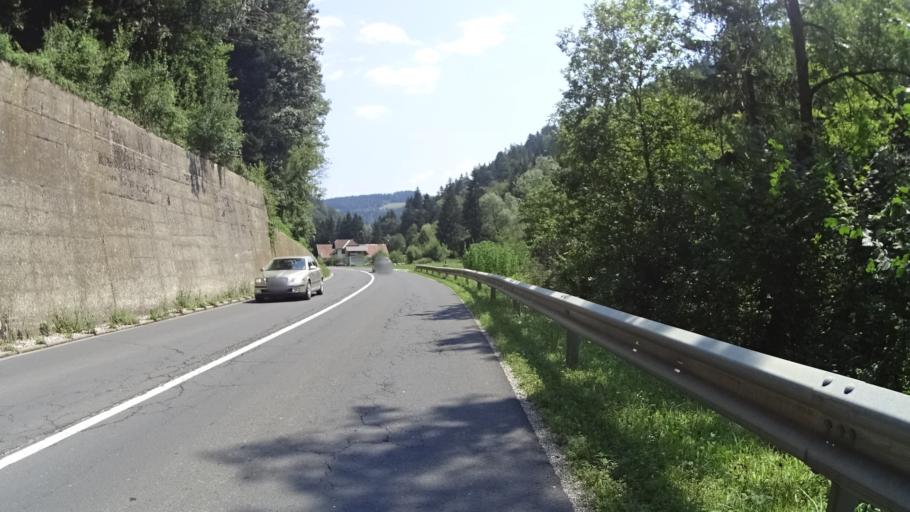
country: SI
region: Prevalje
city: Prevalje
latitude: 46.5476
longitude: 14.8961
